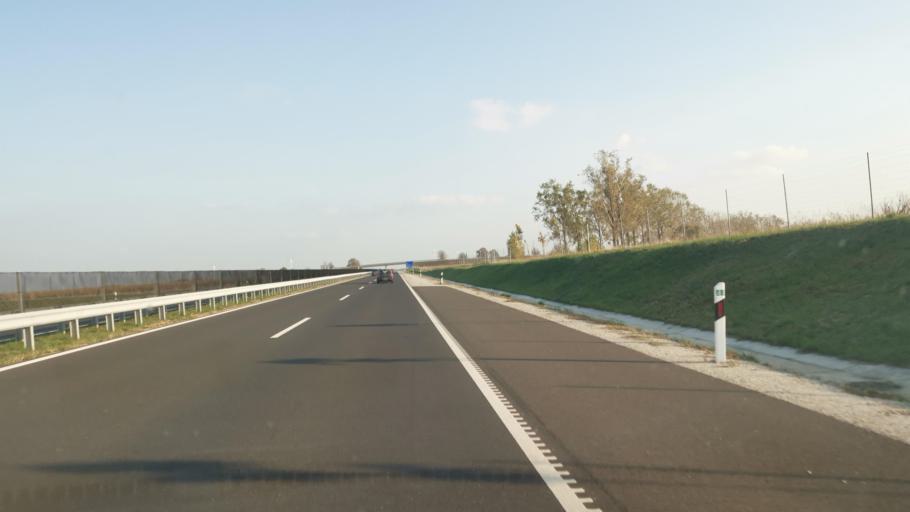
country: HU
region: Gyor-Moson-Sopron
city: Nagycenk
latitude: 47.5889
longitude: 16.7110
